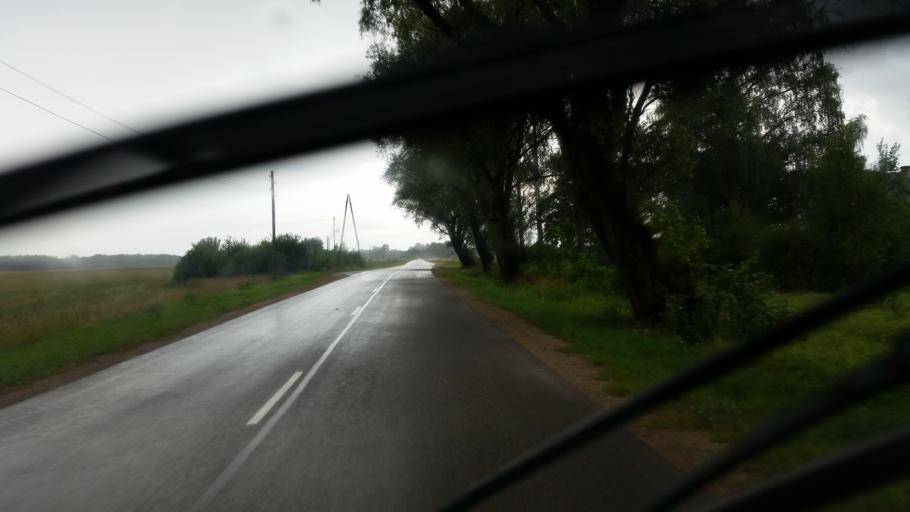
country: LV
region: Vecumnieki
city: Vecumnieki
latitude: 56.4324
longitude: 24.4115
